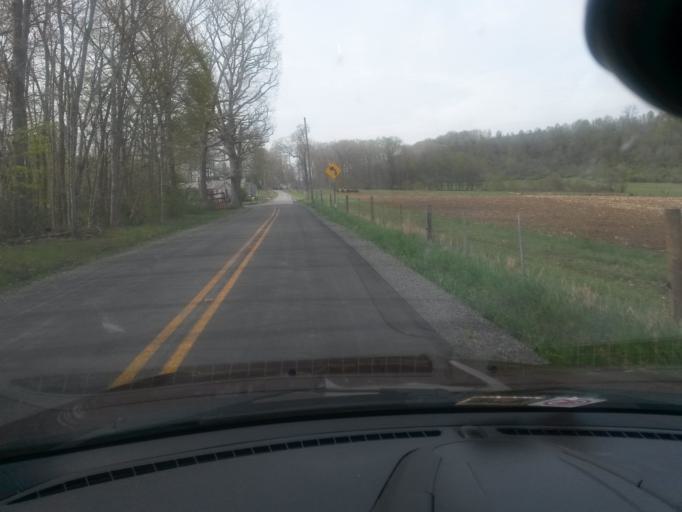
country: US
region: West Virginia
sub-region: Pocahontas County
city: Marlinton
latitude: 38.0935
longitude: -80.2261
